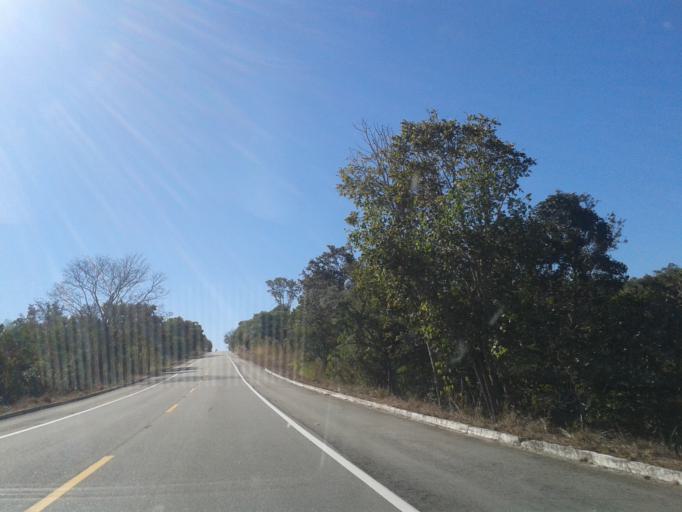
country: BR
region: Goias
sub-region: Goias
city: Goias
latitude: -15.7317
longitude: -50.1848
